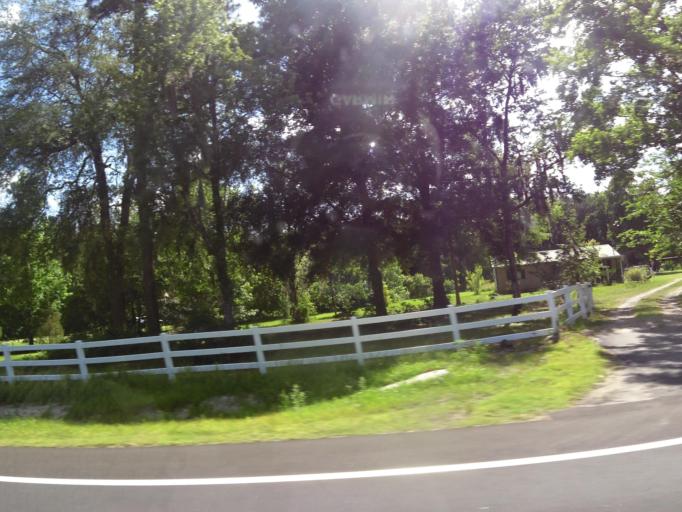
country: US
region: Florida
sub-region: Nassau County
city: Callahan
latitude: 30.5963
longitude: -81.8626
